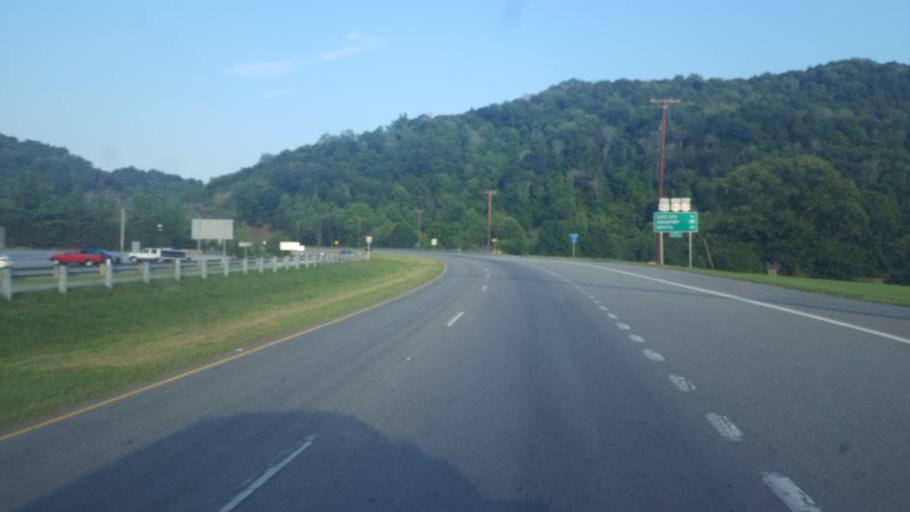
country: US
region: Virginia
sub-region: Lee County
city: Dryden
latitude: 36.7112
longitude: -82.7920
